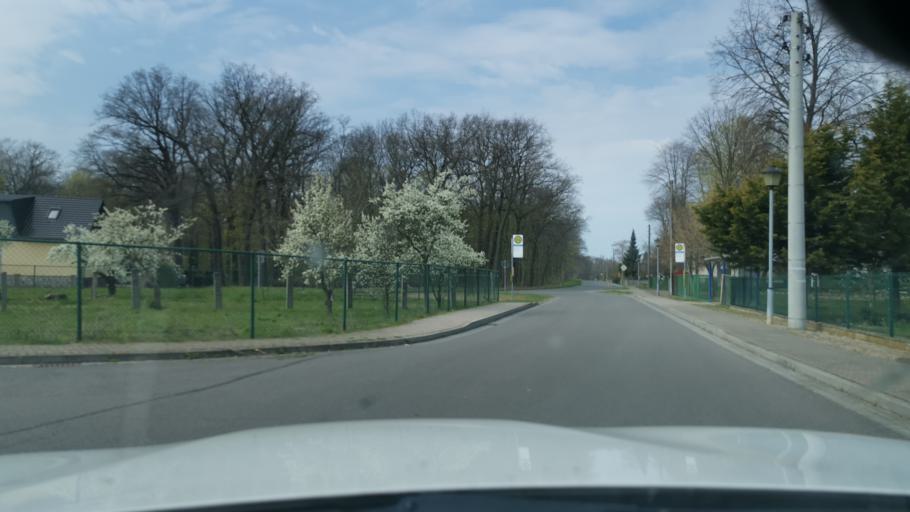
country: DE
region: Saxony
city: Lobnitz
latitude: 51.5566
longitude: 12.4551
